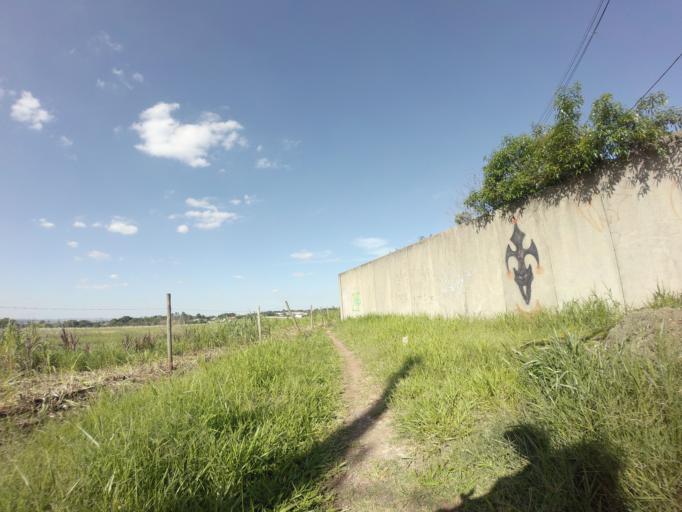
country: BR
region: Sao Paulo
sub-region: Piracicaba
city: Piracicaba
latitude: -22.7494
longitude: -47.5865
